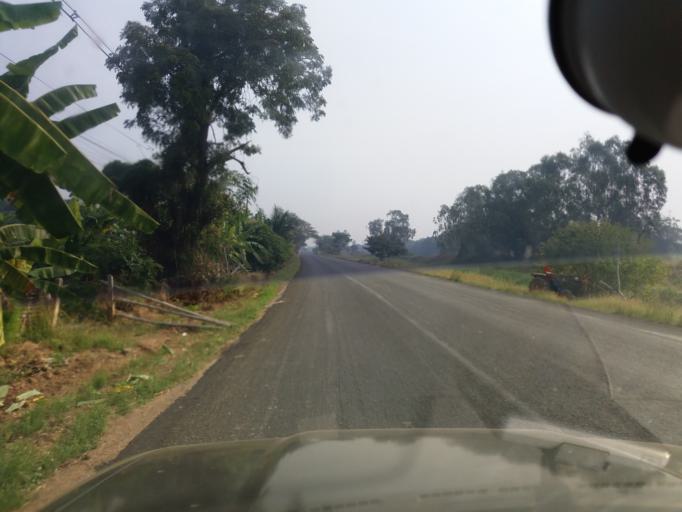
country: TH
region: Sing Buri
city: Bang Racham
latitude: 14.9063
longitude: 100.2035
